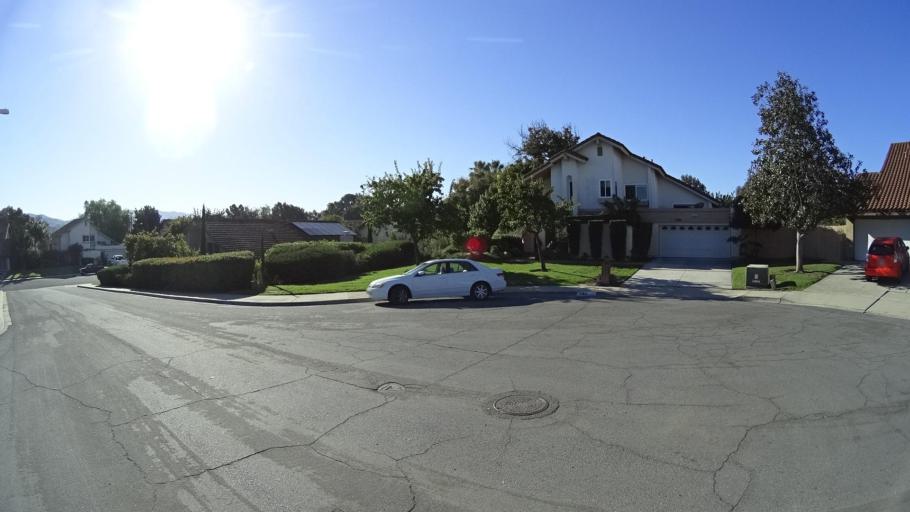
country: US
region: California
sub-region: San Diego County
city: Bonita
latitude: 32.6763
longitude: -117.0282
